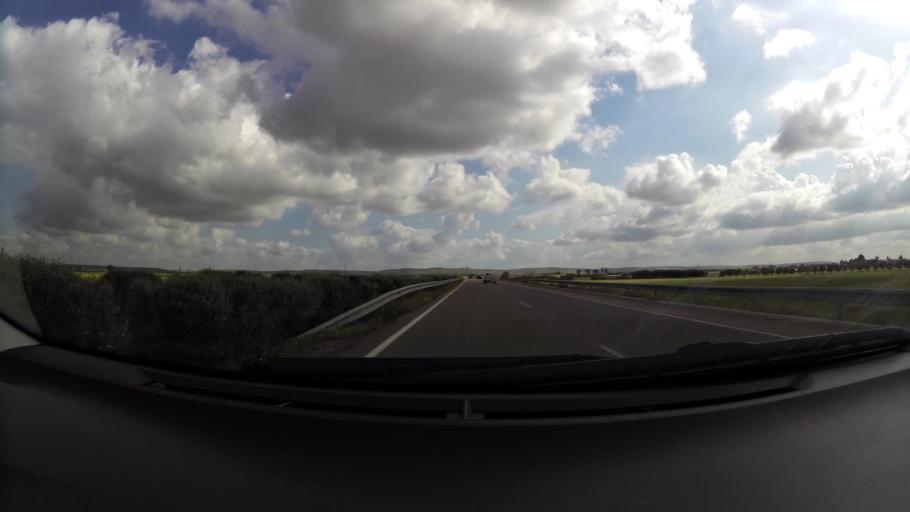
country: MA
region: Chaouia-Ouardigha
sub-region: Settat Province
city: Settat
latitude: 33.1278
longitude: -7.5791
